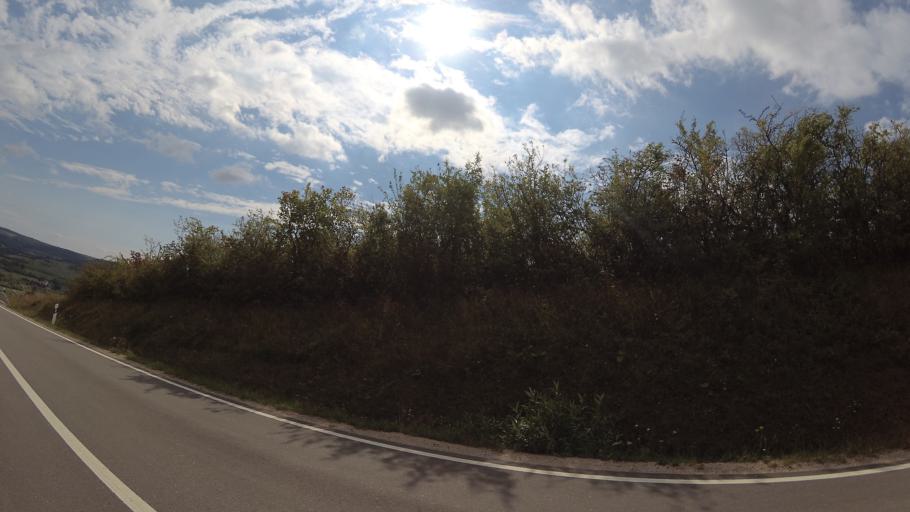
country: FR
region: Lorraine
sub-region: Departement de la Moselle
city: Bliesbruck
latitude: 49.1337
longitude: 7.1656
